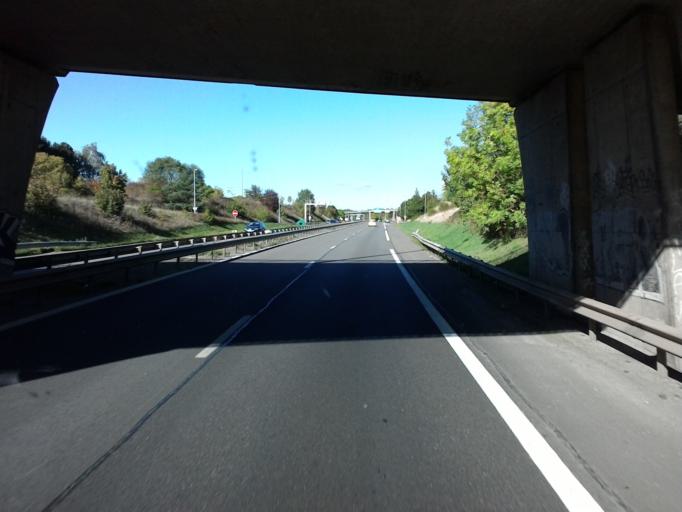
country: FR
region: Lorraine
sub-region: Departement de Meurthe-et-Moselle
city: Longwy
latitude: 49.5277
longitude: 5.7549
